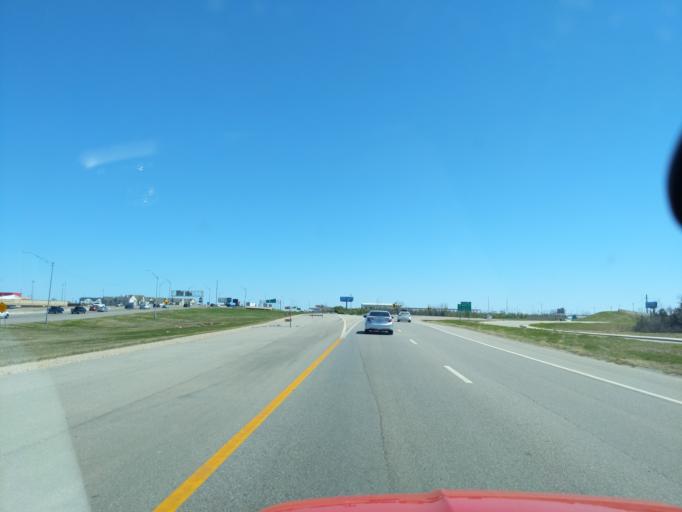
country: US
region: Oklahoma
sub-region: Cleveland County
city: Moore
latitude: 35.3915
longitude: -97.4992
